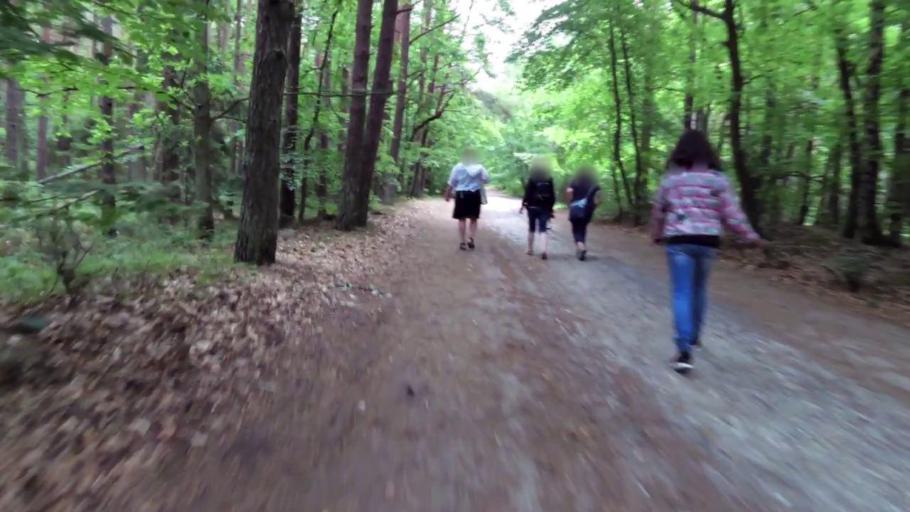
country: PL
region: West Pomeranian Voivodeship
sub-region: Powiat kamienski
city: Miedzyzdroje
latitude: 53.9324
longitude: 14.4662
